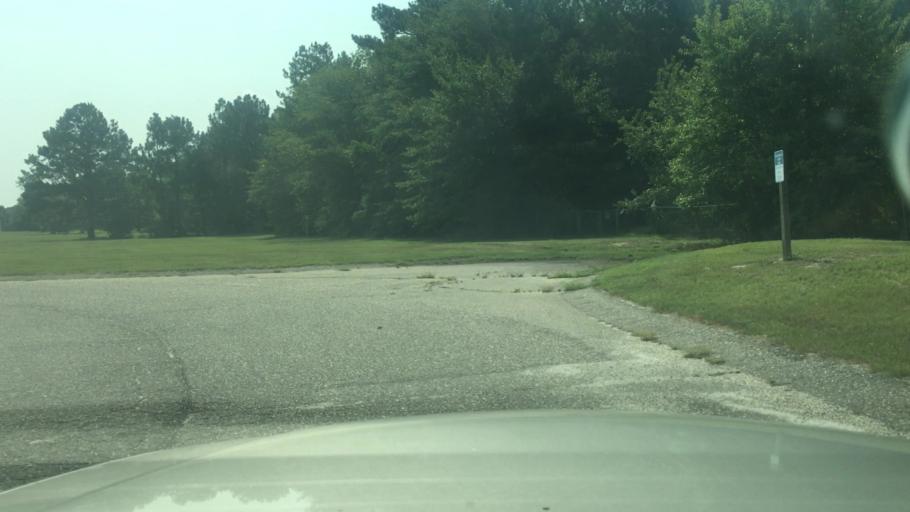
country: US
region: North Carolina
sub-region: Cumberland County
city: Hope Mills
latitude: 34.9967
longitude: -78.9526
